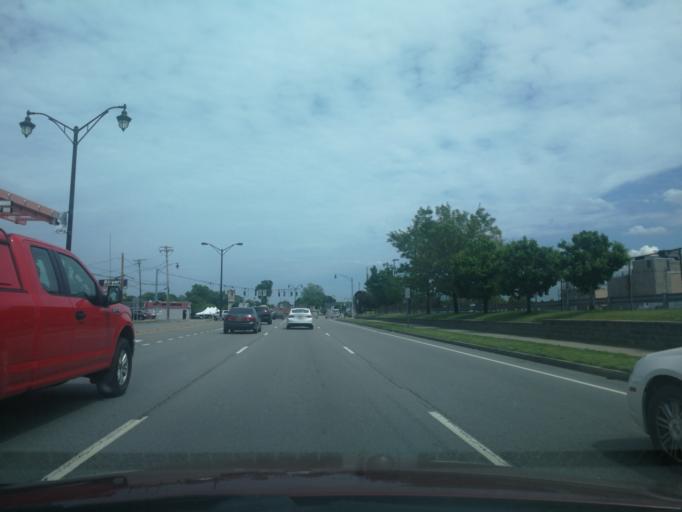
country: US
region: New York
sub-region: Monroe County
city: Greece
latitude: 43.2026
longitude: -77.6462
